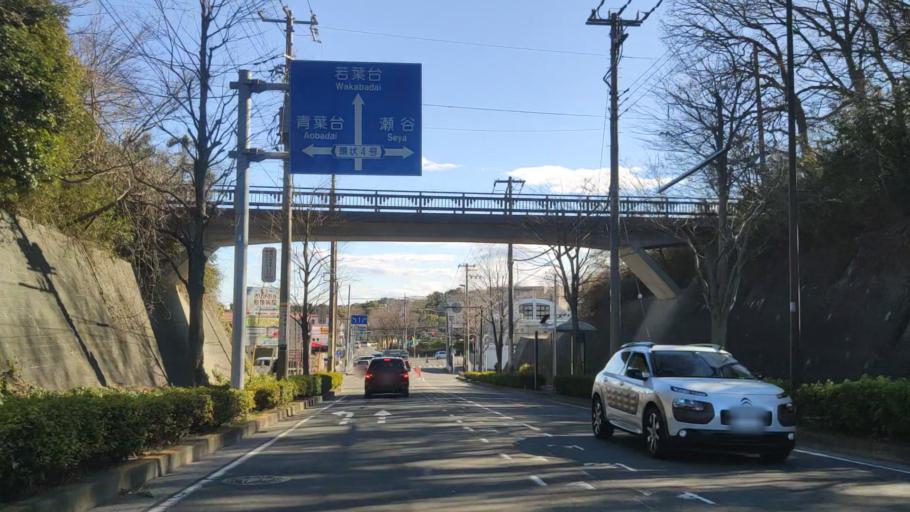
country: JP
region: Tokyo
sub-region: Machida-shi
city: Machida
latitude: 35.5165
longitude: 139.4986
